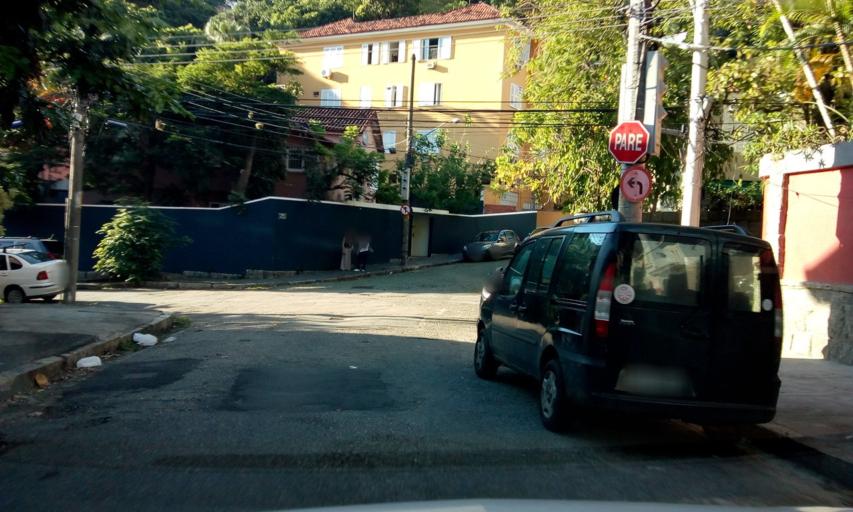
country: BR
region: Rio de Janeiro
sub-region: Rio De Janeiro
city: Rio de Janeiro
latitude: -22.9567
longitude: -43.2024
